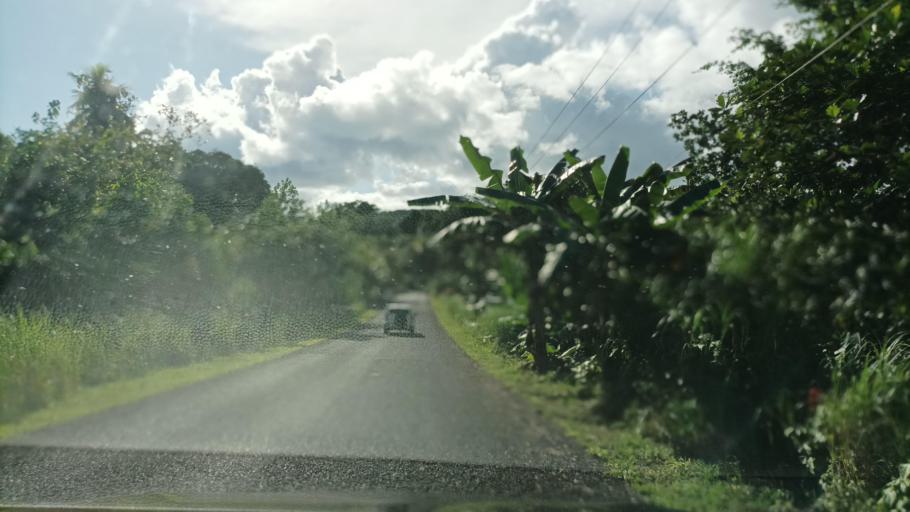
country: FM
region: Pohnpei
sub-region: Sokehs Municipality
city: Palikir - National Government Center
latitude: 6.8239
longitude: 158.1730
